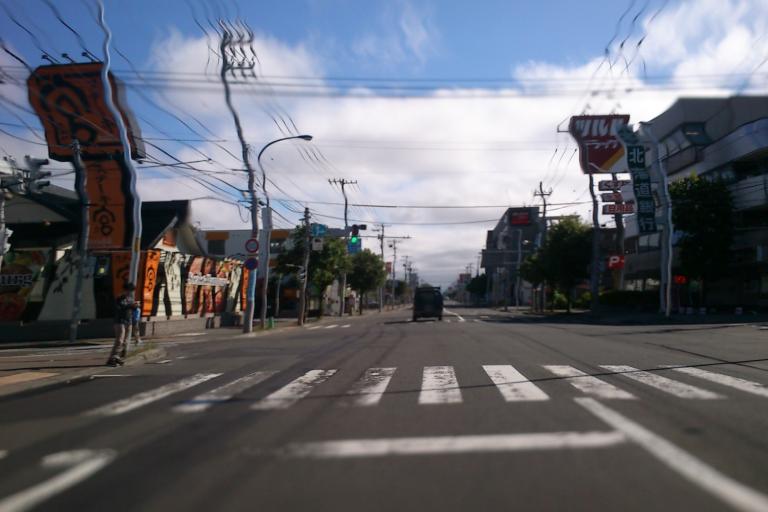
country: JP
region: Hokkaido
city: Sapporo
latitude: 43.1224
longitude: 141.2492
